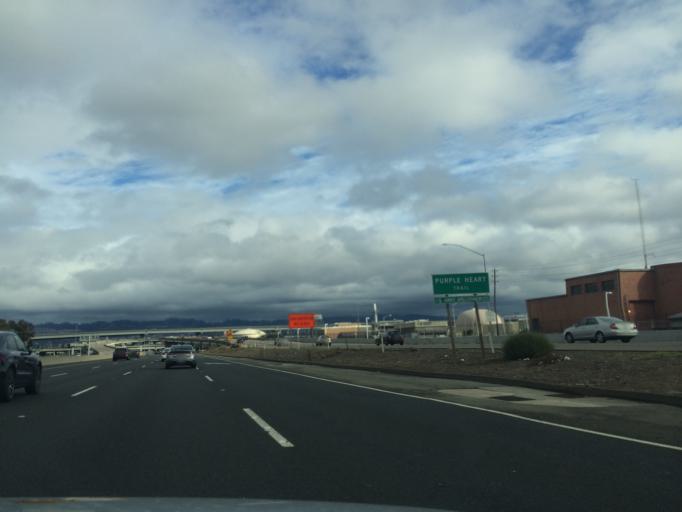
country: US
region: California
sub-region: Alameda County
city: Emeryville
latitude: 37.8262
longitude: -122.3002
